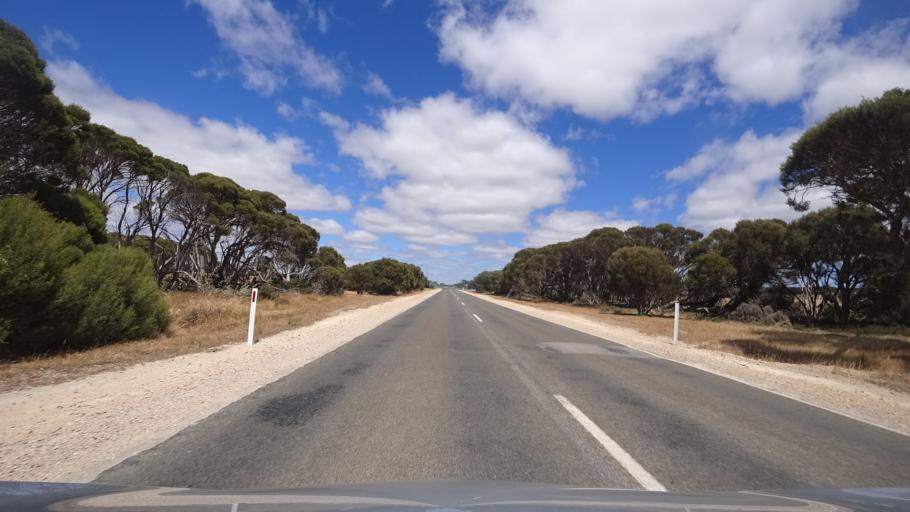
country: AU
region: South Australia
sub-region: Kangaroo Island
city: Kingscote
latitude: -35.6772
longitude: 137.5779
